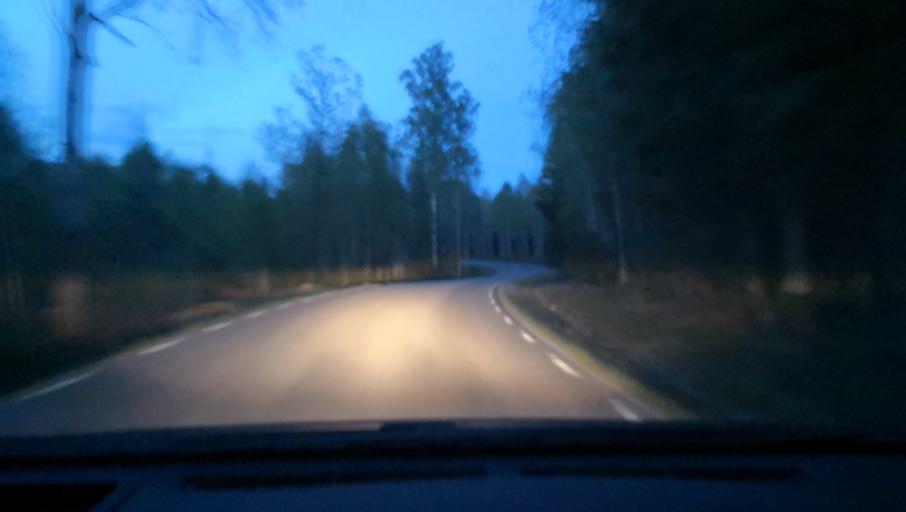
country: SE
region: OErebro
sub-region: Orebro Kommun
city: Vintrosa
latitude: 59.1890
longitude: 15.0458
